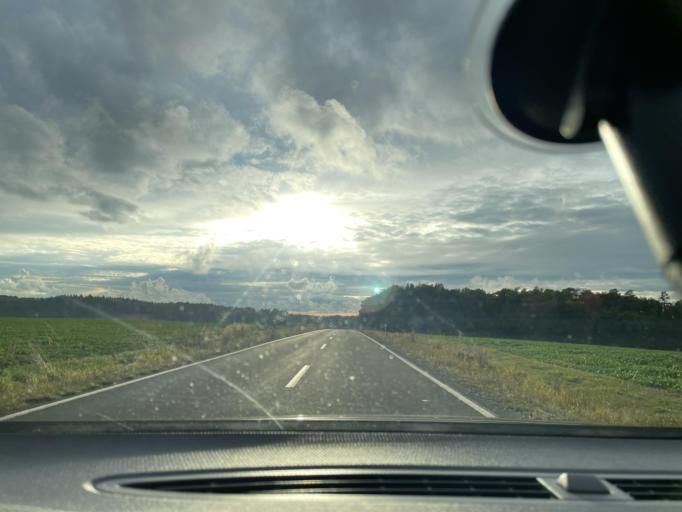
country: DE
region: Bavaria
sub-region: Regierungsbezirk Unterfranken
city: Rodelmaier
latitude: 50.2951
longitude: 10.2681
